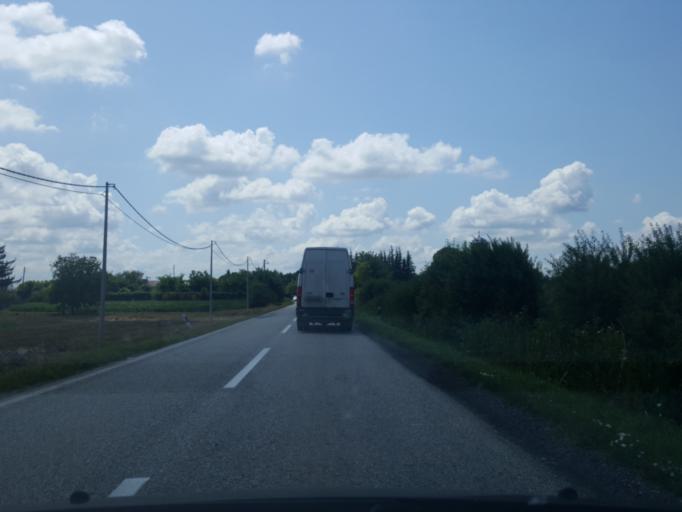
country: RS
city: Glusci
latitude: 44.9001
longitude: 19.5453
